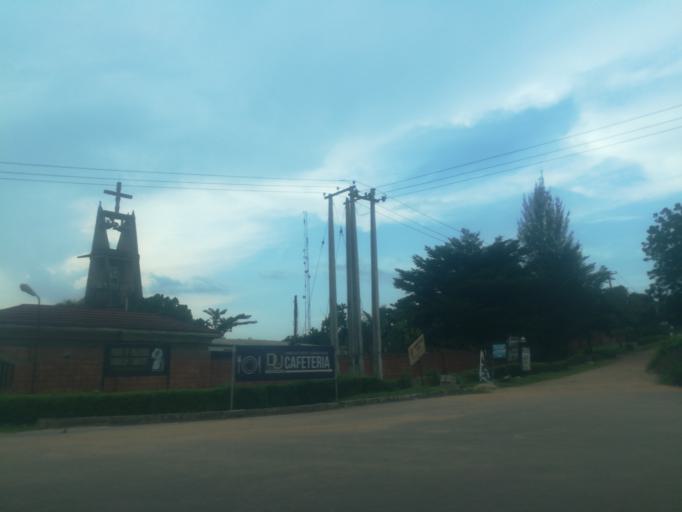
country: NG
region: Oyo
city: Ibadan
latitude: 7.4332
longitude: 3.9023
